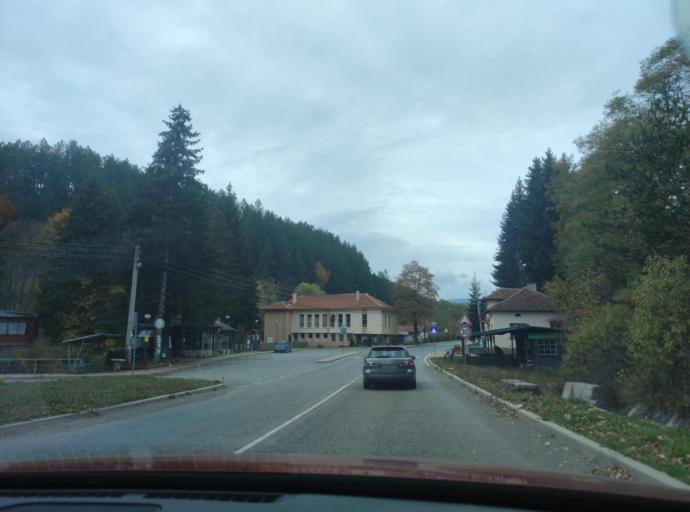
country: BG
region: Sofiya
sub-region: Obshtina Godech
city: Godech
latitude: 43.0723
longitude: 23.1087
